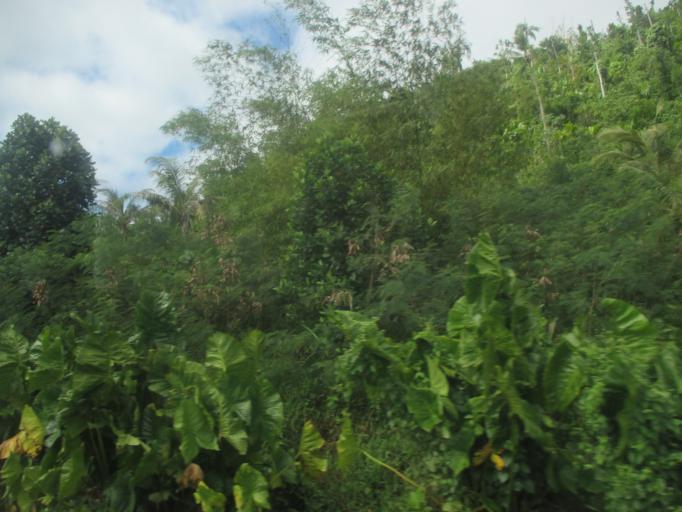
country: PH
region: Eastern Visayas
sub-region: Province of Eastern Samar
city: Lawa-an
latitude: 11.1106
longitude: 125.2453
